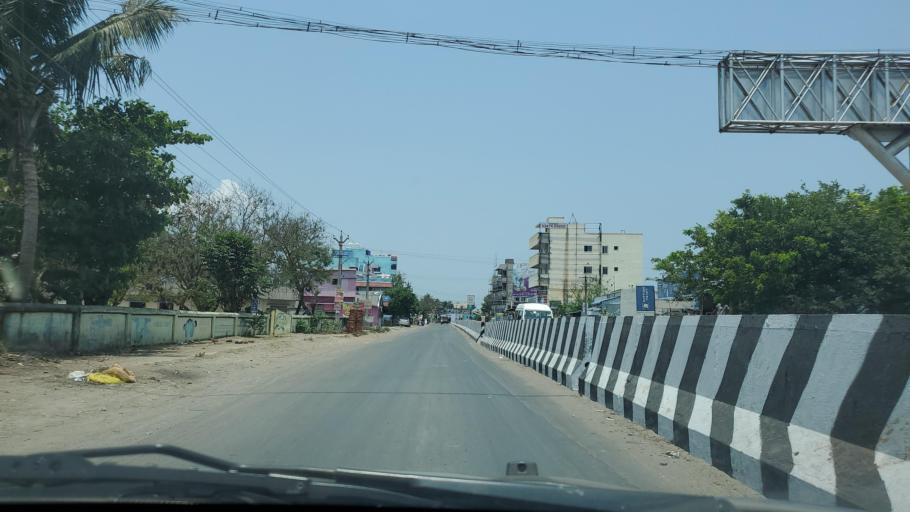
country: IN
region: Tamil Nadu
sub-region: Kancheepuram
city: Vengavasal
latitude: 12.8570
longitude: 80.1722
